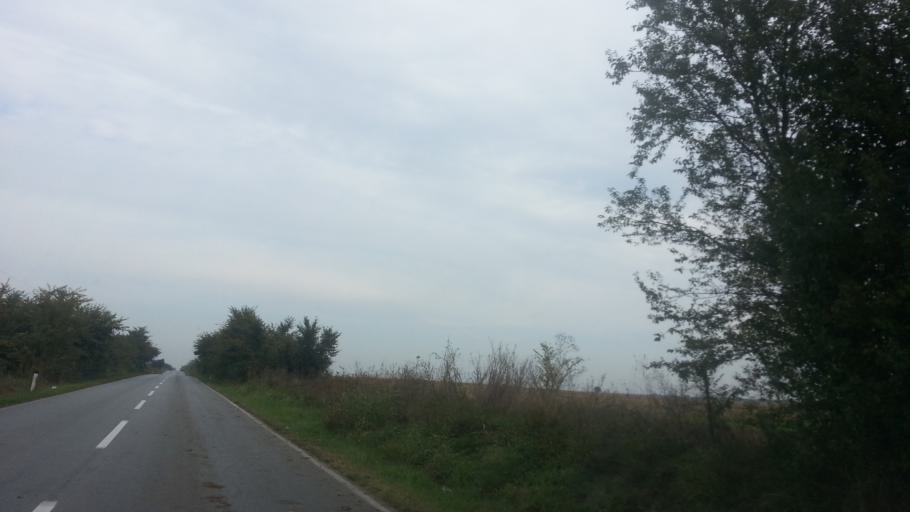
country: RS
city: Belegis
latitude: 45.0463
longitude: 20.3324
